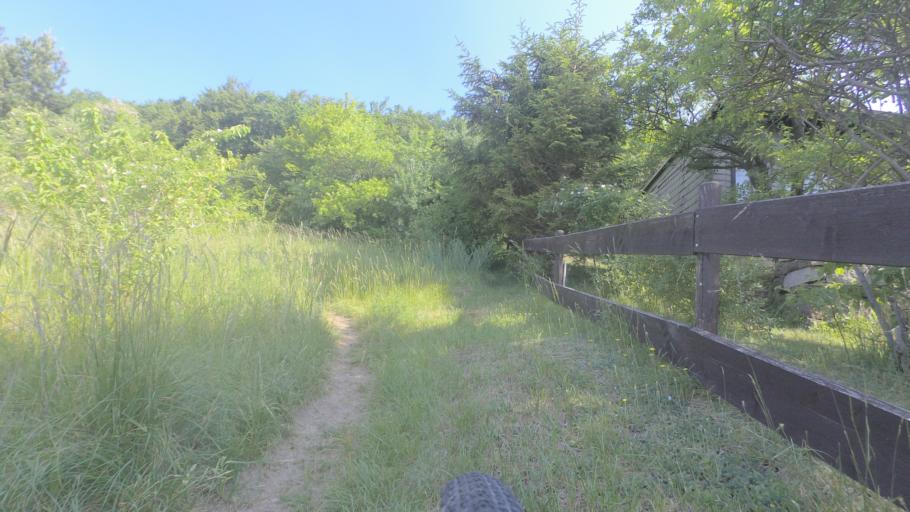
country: DE
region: Saxony-Anhalt
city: Derenburg
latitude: 51.8370
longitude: 10.8591
